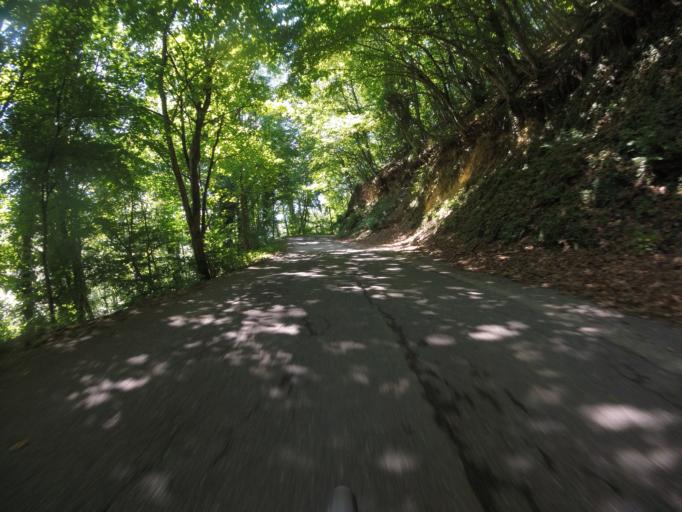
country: SI
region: Brezice
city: Brezice
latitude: 45.8266
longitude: 15.5552
